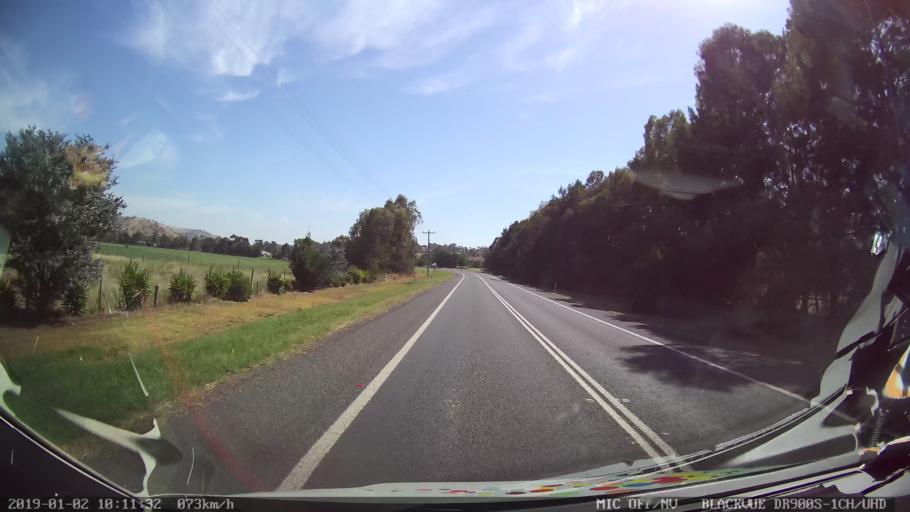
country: AU
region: New South Wales
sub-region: Gundagai
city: Gundagai
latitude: -35.0921
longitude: 148.0929
